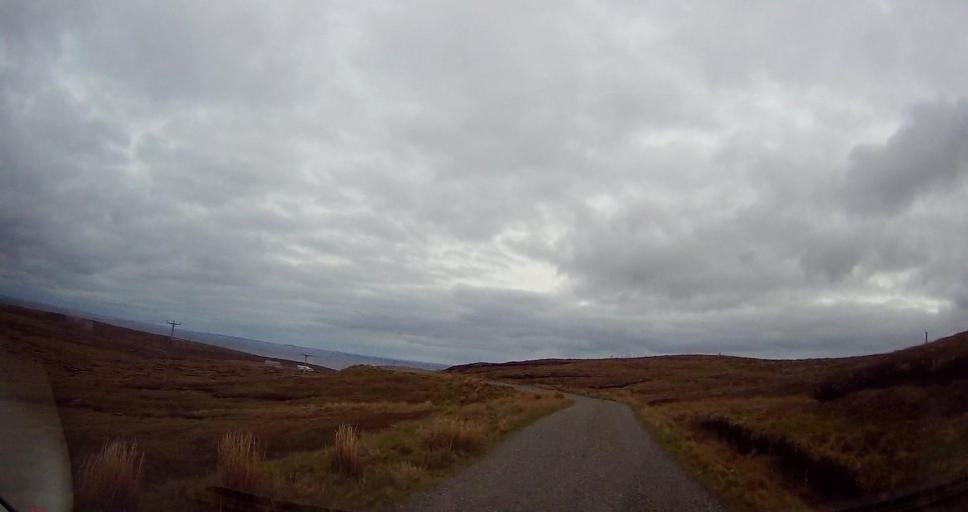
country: GB
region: Scotland
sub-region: Shetland Islands
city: Shetland
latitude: 60.5630
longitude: -1.0638
